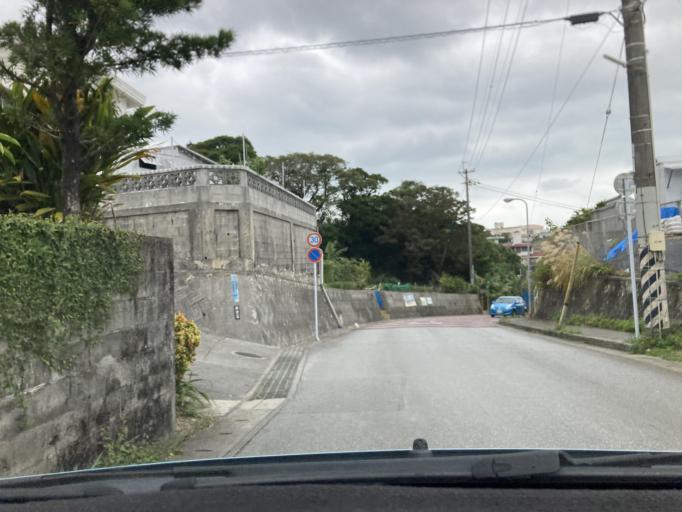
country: JP
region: Okinawa
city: Okinawa
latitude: 26.3440
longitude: 127.8074
